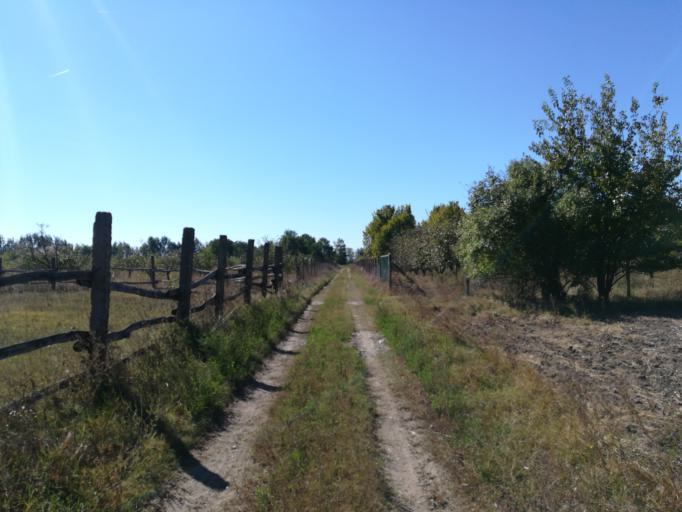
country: HU
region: Bacs-Kiskun
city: Tiszakecske
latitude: 46.9456
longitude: 20.0751
